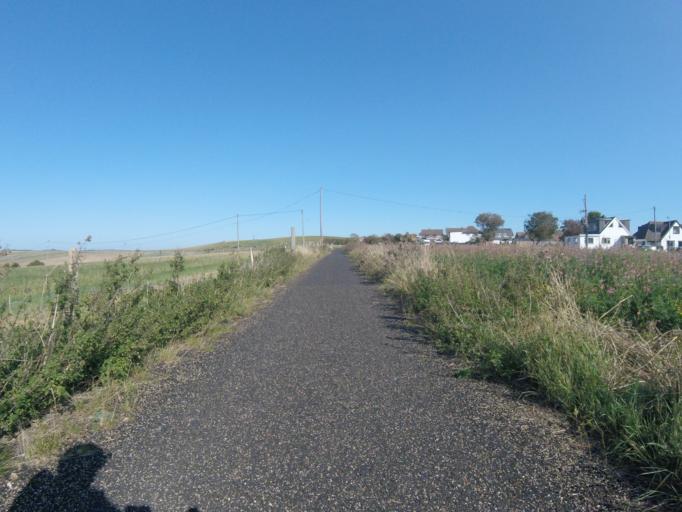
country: GB
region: England
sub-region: Brighton and Hove
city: Rottingdean
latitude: 50.8379
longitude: -0.0830
